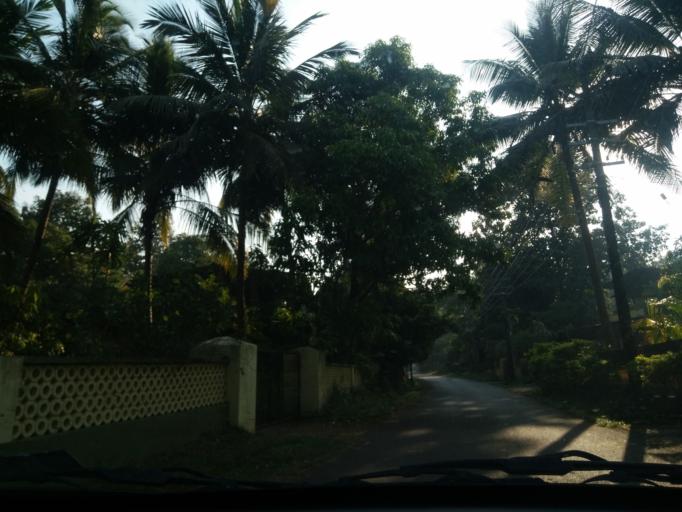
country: IN
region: Goa
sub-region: South Goa
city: Chinchinim
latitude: 15.2042
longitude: 73.9850
